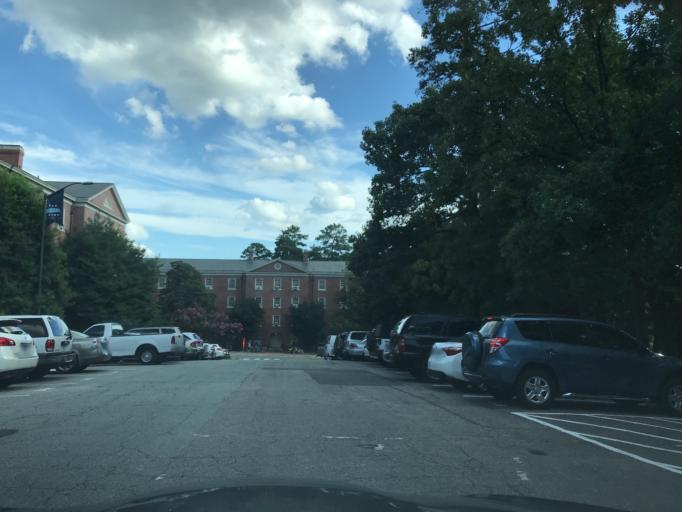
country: US
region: North Carolina
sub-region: Orange County
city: Chapel Hill
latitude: 35.9071
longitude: -79.0448
